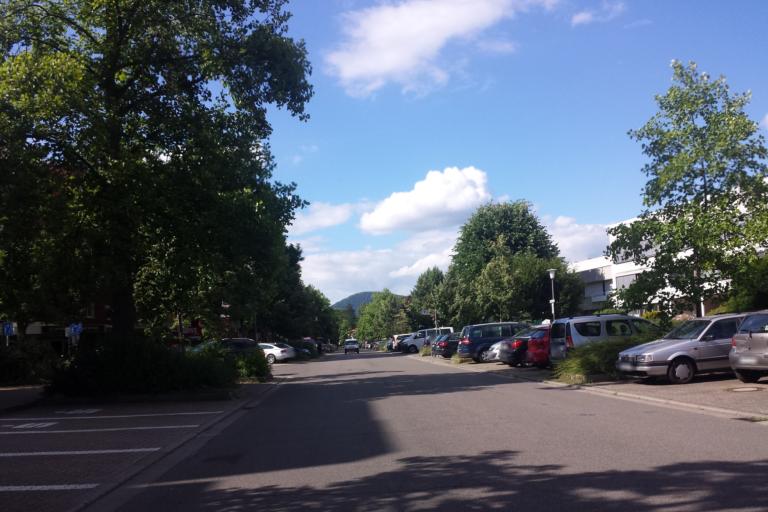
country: DE
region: Baden-Wuerttemberg
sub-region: Karlsruhe Region
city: Heidelberg
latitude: 49.4208
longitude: 8.6806
